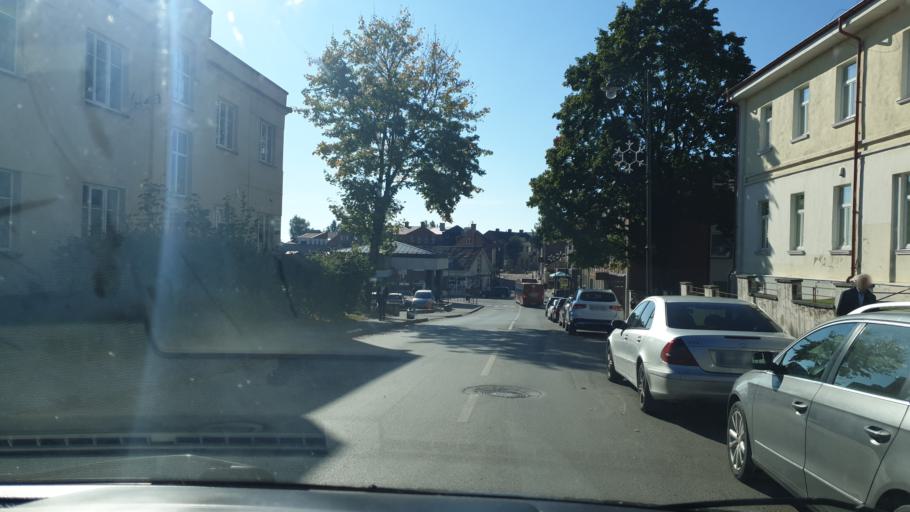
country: LT
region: Telsiu apskritis
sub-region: Telsiai
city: Telsiai
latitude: 55.9847
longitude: 22.2496
